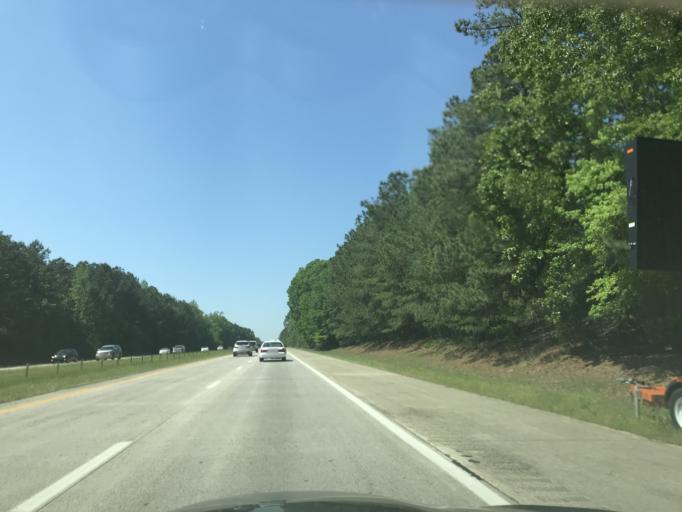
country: US
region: North Carolina
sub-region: Johnston County
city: Benson
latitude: 35.5265
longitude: -78.5648
